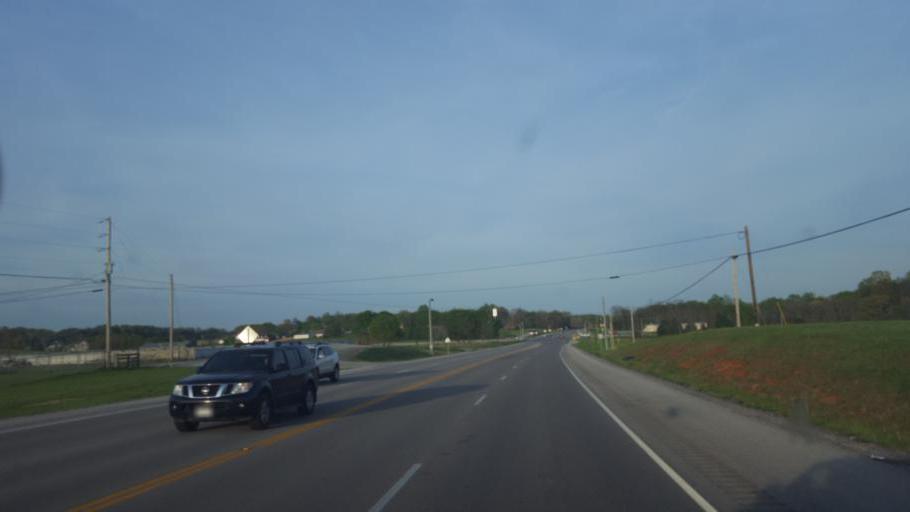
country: US
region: Kentucky
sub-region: Barren County
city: Glasgow
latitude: 37.0088
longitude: -85.8852
